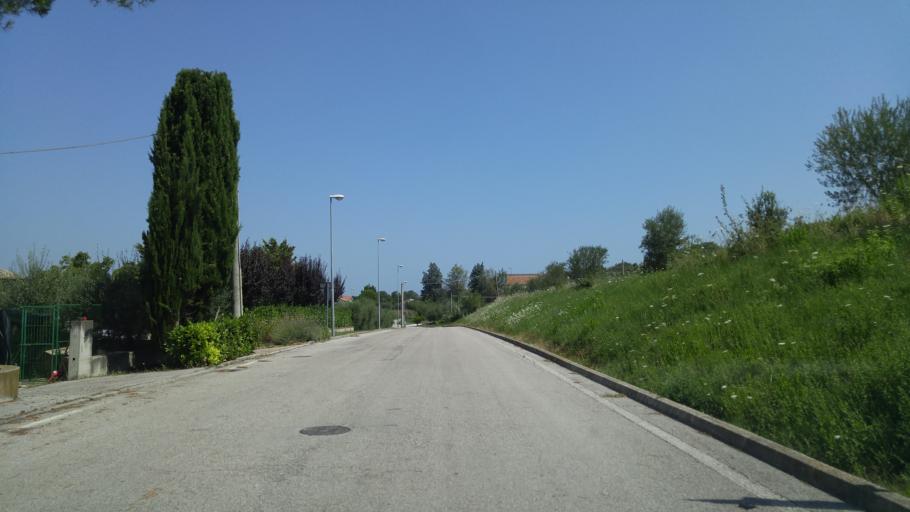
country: IT
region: The Marches
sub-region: Provincia di Pesaro e Urbino
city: Piagge
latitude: 43.7541
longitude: 12.9686
